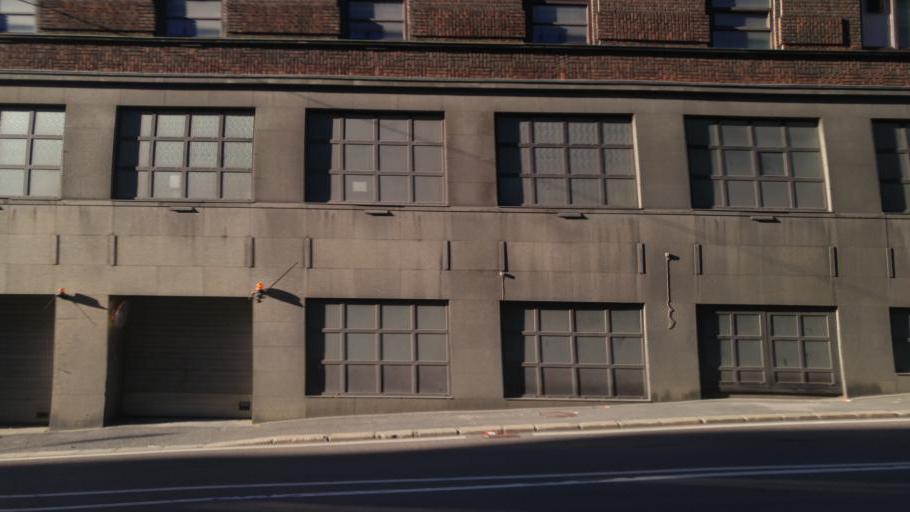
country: NO
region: Oslo
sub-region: Oslo
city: Oslo
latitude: 59.9162
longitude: 10.7482
